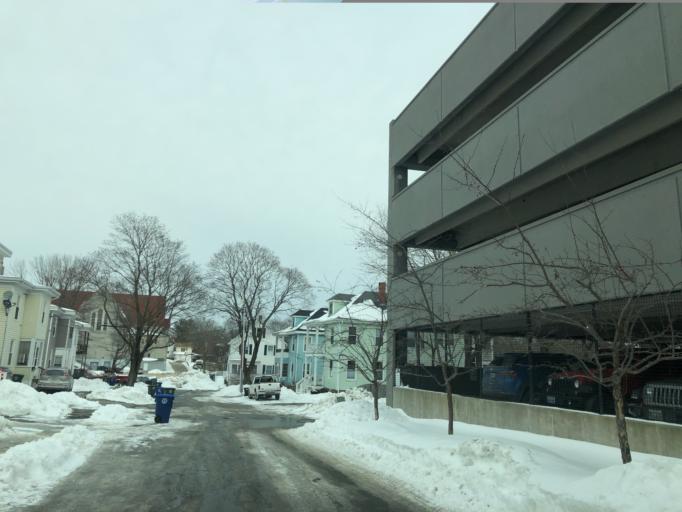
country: US
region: Maine
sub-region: Cumberland County
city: Westbrook
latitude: 43.6788
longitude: -70.3662
